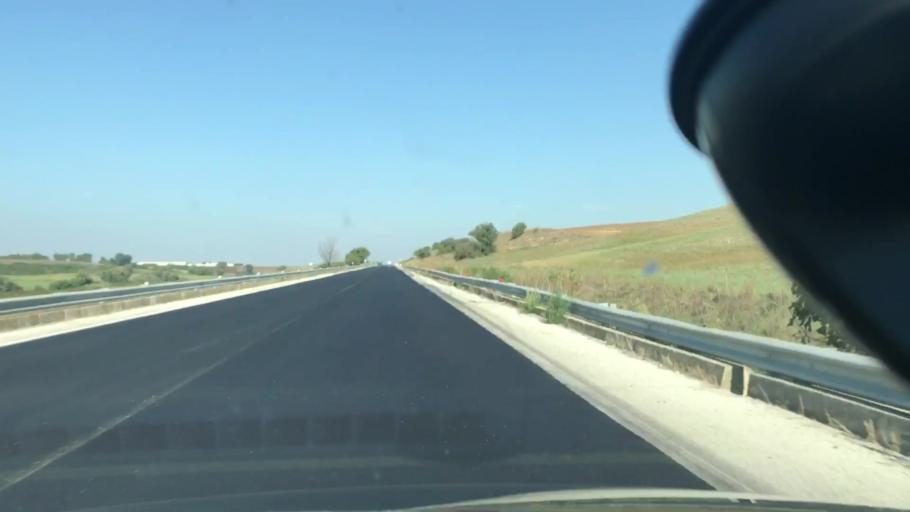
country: IT
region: Apulia
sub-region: Provincia di Barletta - Andria - Trani
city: Spinazzola
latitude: 40.9038
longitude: 16.1161
